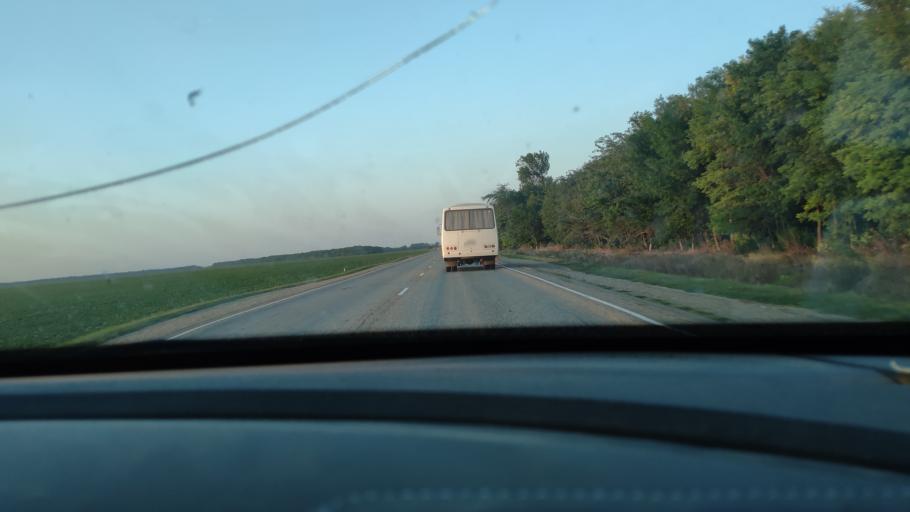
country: RU
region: Krasnodarskiy
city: Starominskaya
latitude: 46.4533
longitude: 39.0318
